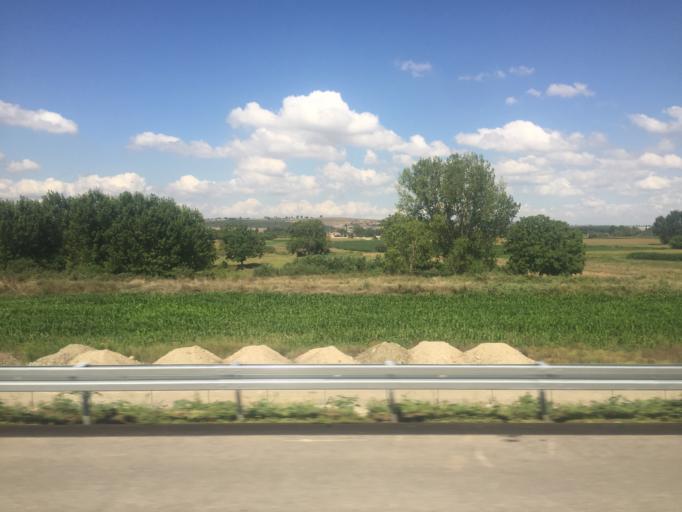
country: TR
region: Balikesir
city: Gobel
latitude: 39.9919
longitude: 28.1889
